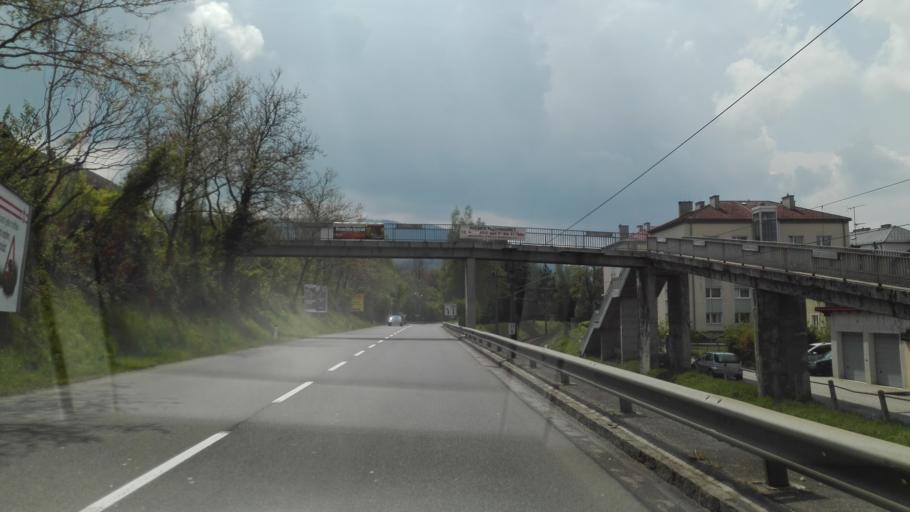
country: AT
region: Upper Austria
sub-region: Politischer Bezirk Steyr-Land
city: Sankt Ulrich bei Steyr
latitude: 48.0292
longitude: 14.4189
